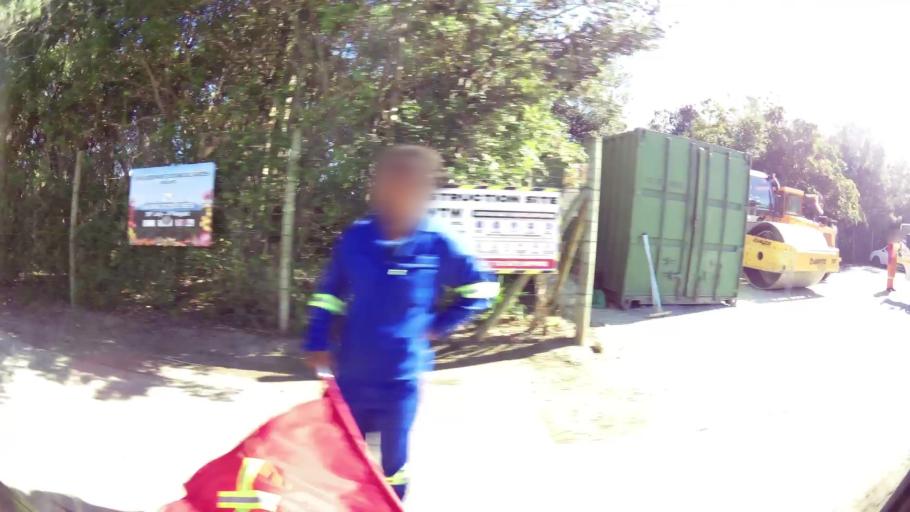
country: ZA
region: Western Cape
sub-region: Eden District Municipality
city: George
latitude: -33.9471
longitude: 22.4648
